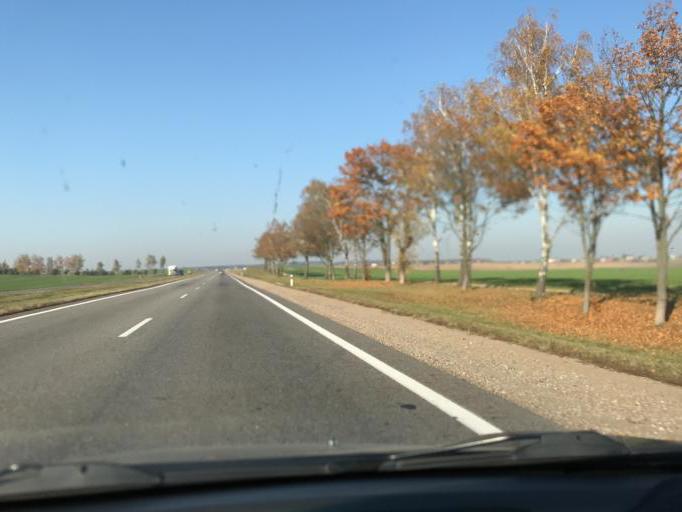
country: BY
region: Minsk
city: Luhavaya Slabada
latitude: 53.7410
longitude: 27.8427
